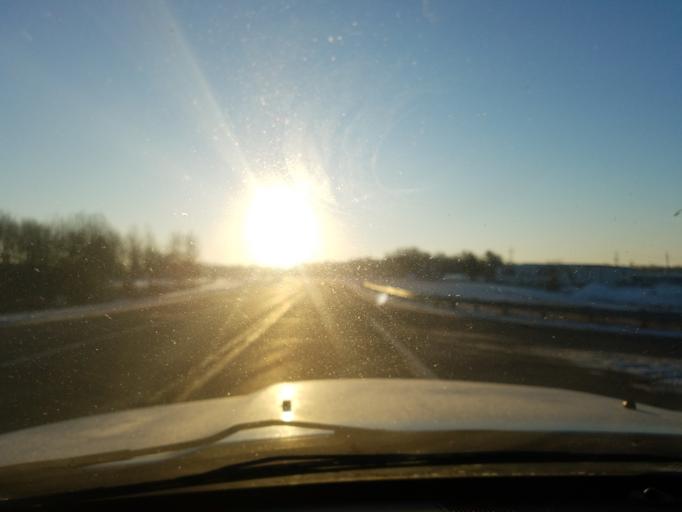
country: US
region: Indiana
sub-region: Marshall County
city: Bremen
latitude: 41.4557
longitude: -86.1342
